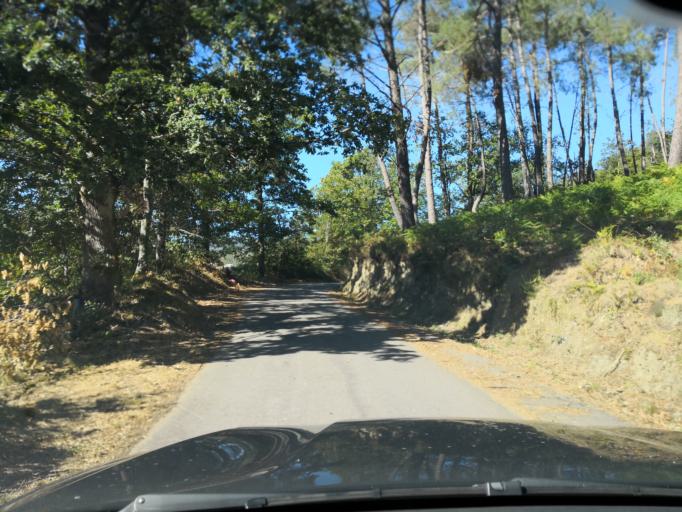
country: PT
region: Vila Real
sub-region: Santa Marta de Penaguiao
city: Santa Marta de Penaguiao
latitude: 41.2953
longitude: -7.8663
